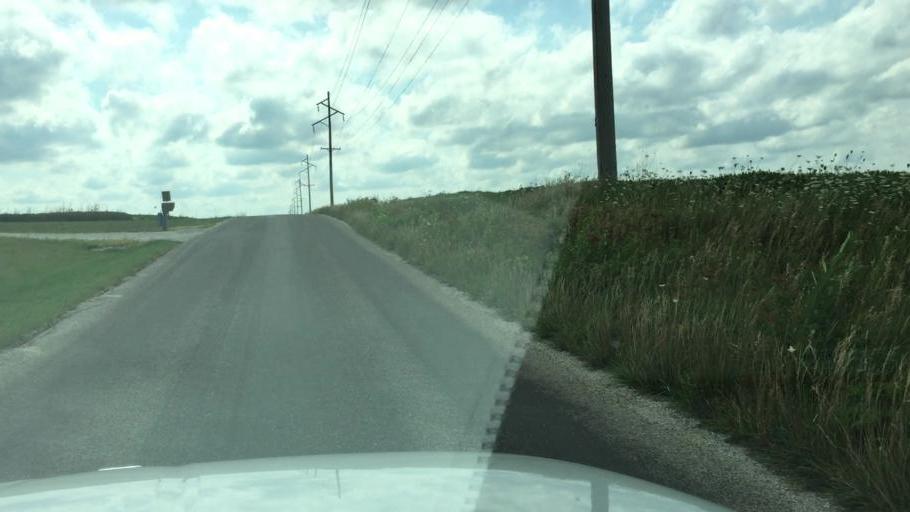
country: US
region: Illinois
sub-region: Hancock County
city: Carthage
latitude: 40.4168
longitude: -91.1654
